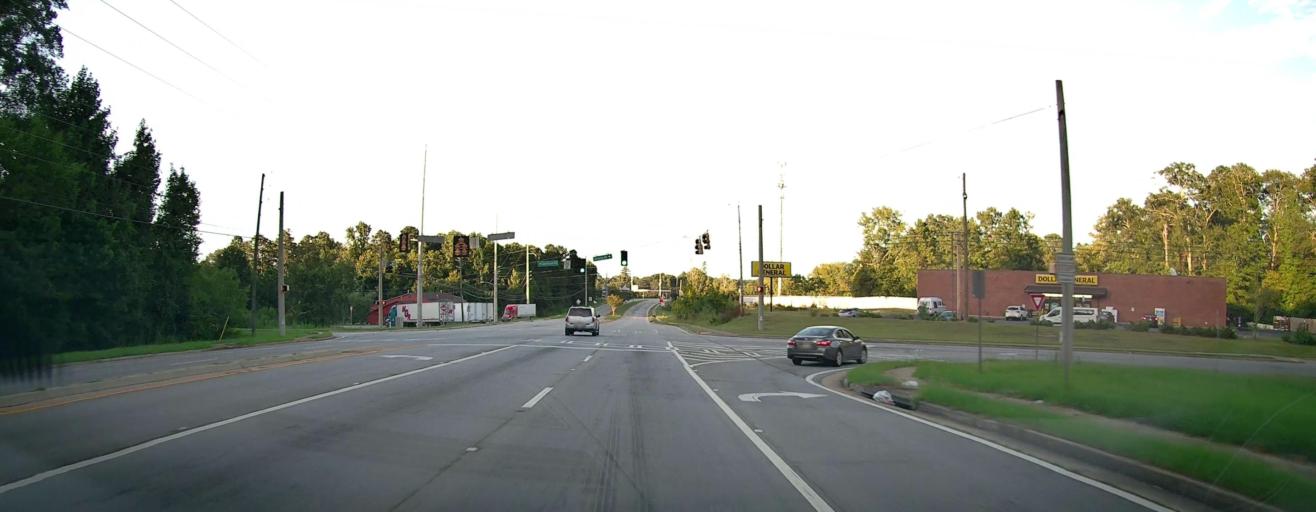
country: US
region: Georgia
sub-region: Muscogee County
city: Columbus
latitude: 32.5132
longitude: -84.8889
